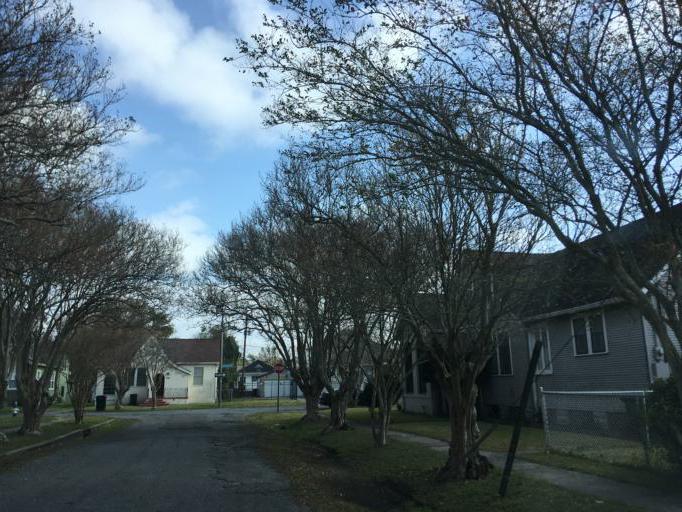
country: US
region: Louisiana
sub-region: Orleans Parish
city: New Orleans
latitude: 29.9976
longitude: -90.0573
